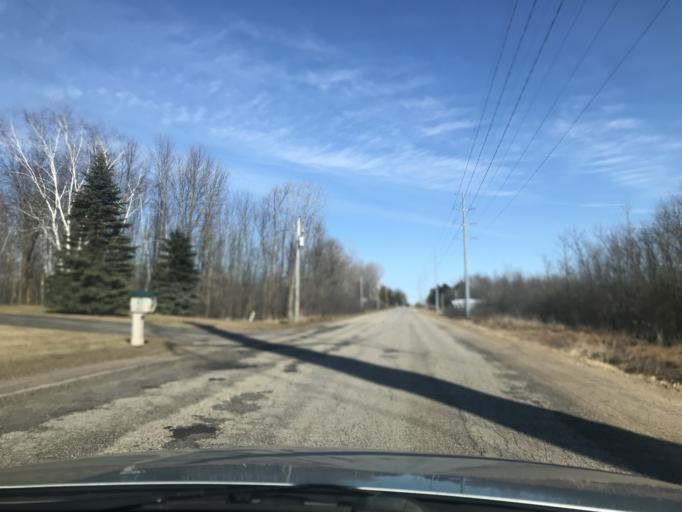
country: US
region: Wisconsin
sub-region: Marinette County
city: Marinette
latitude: 45.1450
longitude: -87.6521
